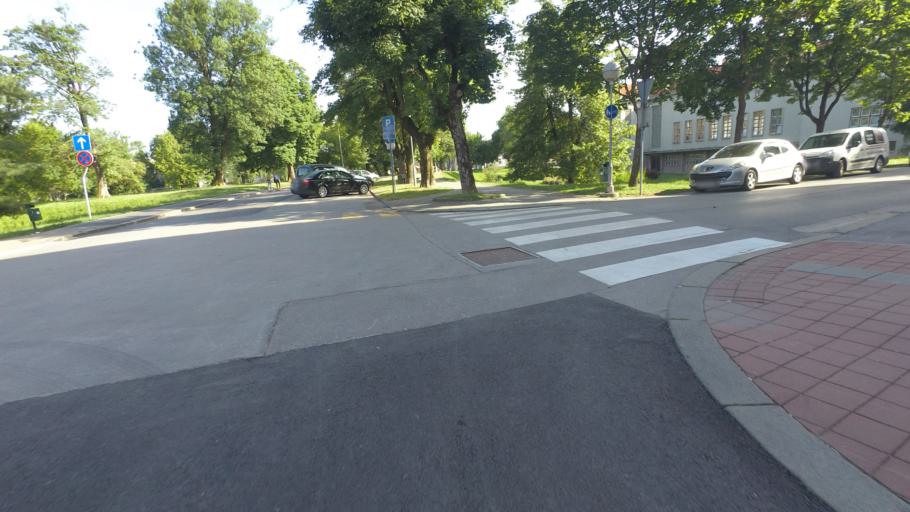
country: HR
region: Karlovacka
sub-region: Grad Karlovac
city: Karlovac
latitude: 45.4913
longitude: 15.5559
